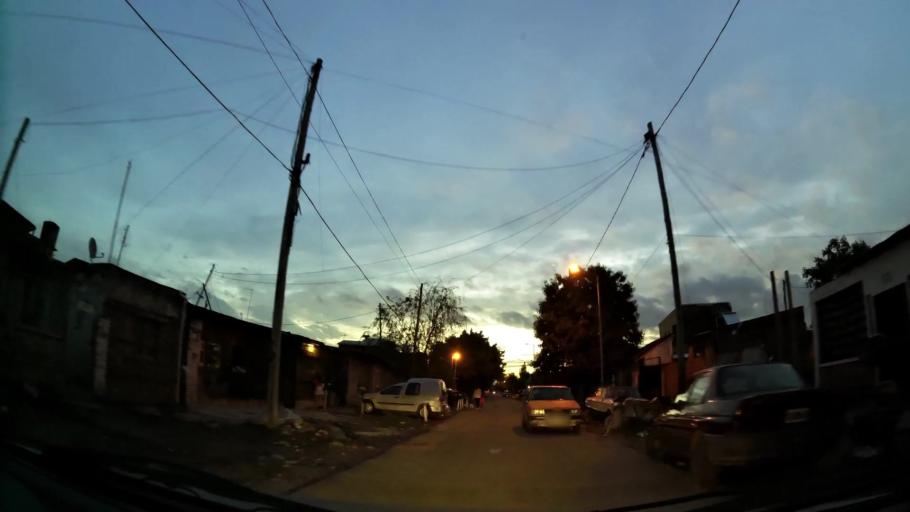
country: AR
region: Buenos Aires
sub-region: Partido de Lomas de Zamora
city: Lomas de Zamora
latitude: -34.7456
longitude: -58.3584
